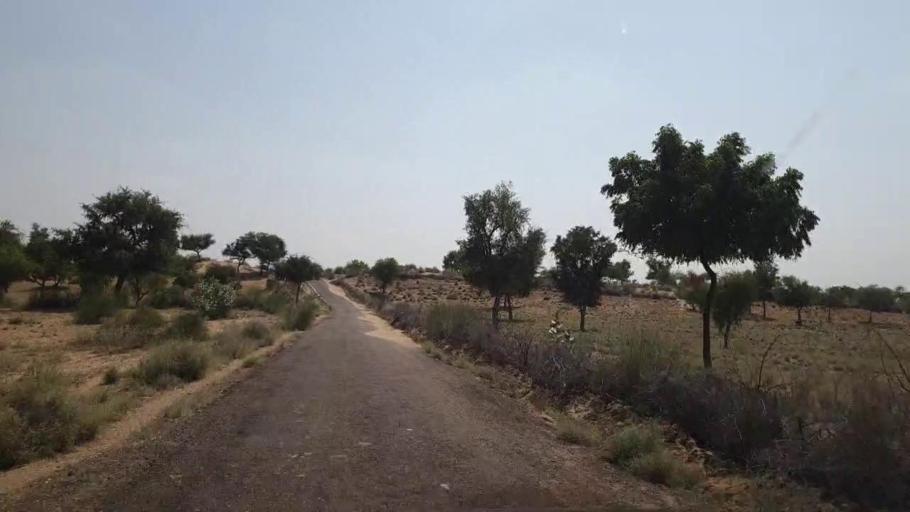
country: PK
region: Sindh
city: Islamkot
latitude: 25.0819
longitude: 70.7363
